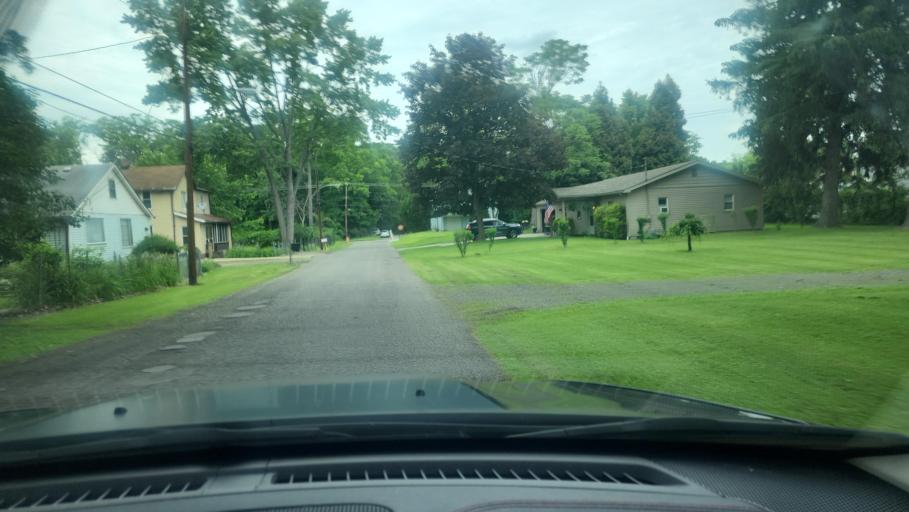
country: US
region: Ohio
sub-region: Trumbull County
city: Niles
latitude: 41.1744
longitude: -80.7763
